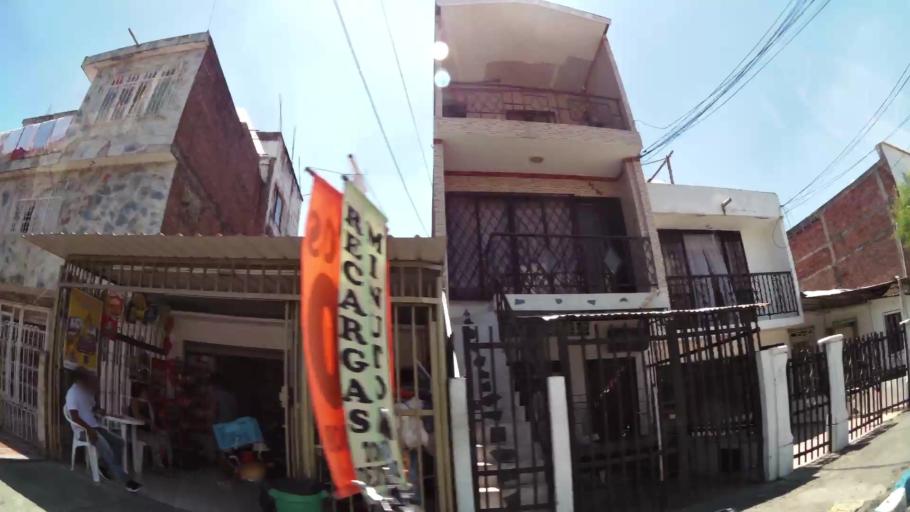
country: CO
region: Valle del Cauca
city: Cali
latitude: 3.4364
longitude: -76.5013
